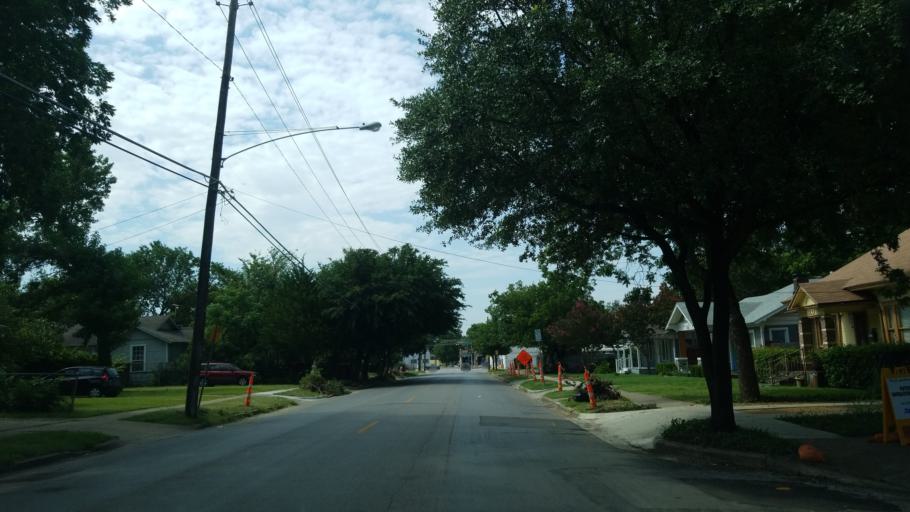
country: US
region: Texas
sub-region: Dallas County
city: Highland Park
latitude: 32.8131
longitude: -96.7748
